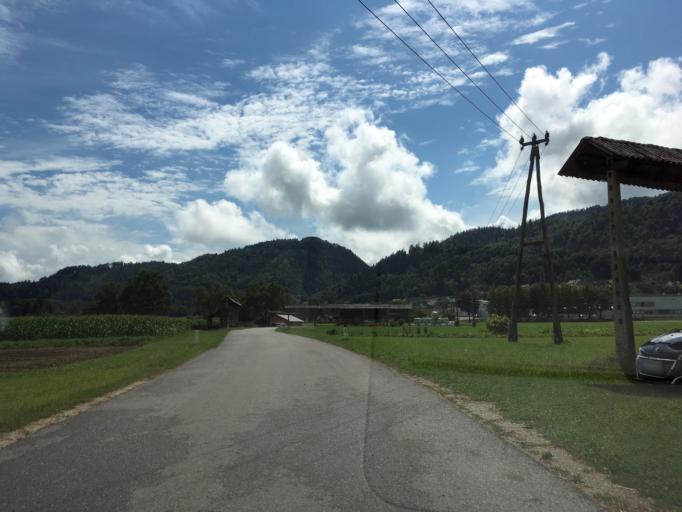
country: SI
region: Bled
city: Zasip
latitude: 46.4116
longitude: 14.1041
